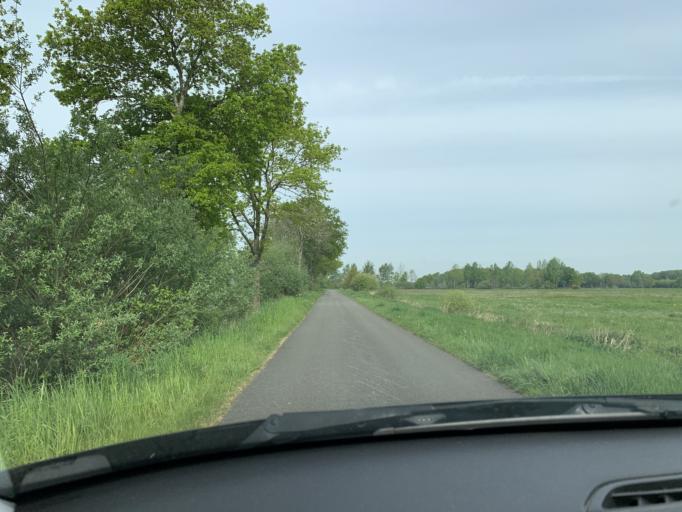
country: DE
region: Lower Saxony
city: Apen
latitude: 53.2397
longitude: 7.8300
